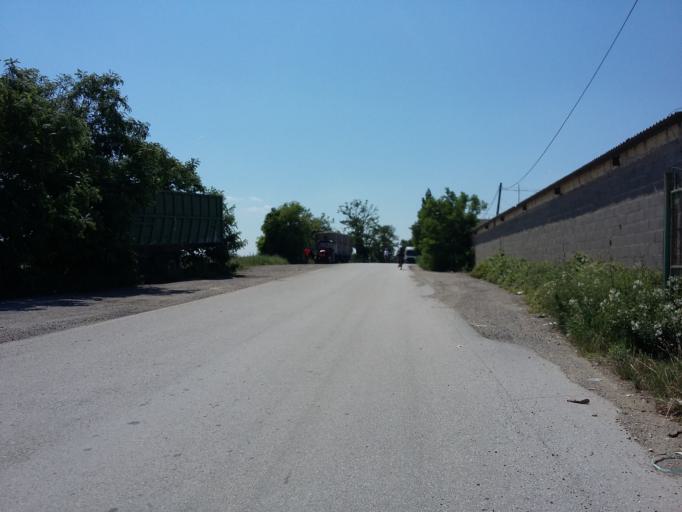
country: AT
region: Lower Austria
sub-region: Politischer Bezirk Ganserndorf
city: Marchegg
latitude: 48.2958
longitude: 16.9681
